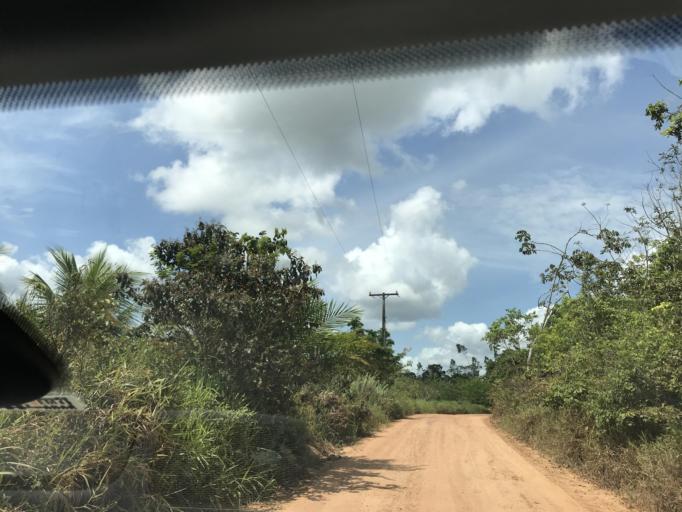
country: BR
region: Bahia
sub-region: Entre Rios
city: Entre Rios
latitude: -12.2218
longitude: -38.0856
